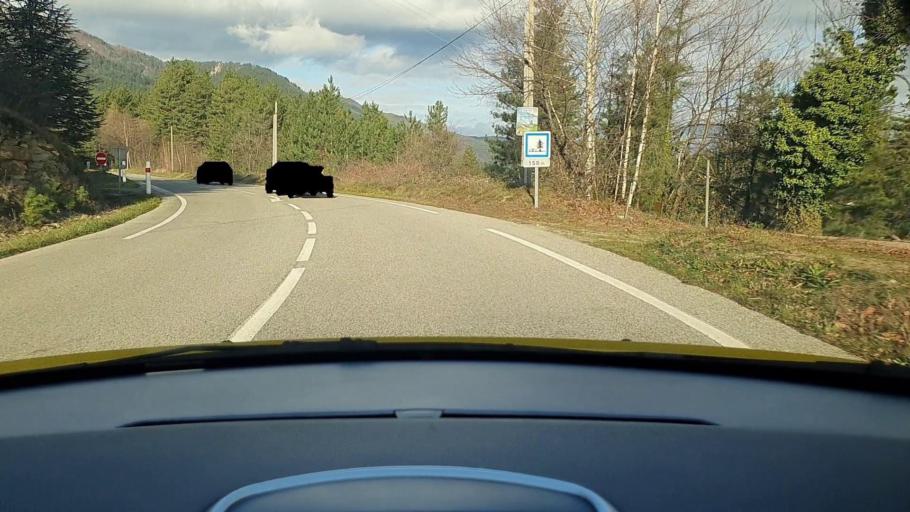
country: FR
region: Languedoc-Roussillon
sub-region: Departement du Gard
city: Branoux-les-Taillades
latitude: 44.3694
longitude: 3.9472
